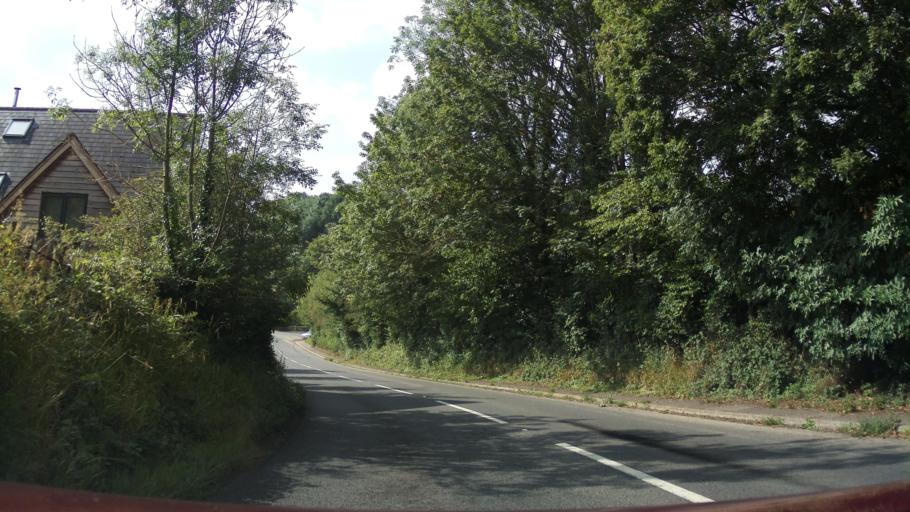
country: GB
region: England
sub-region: Somerset
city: Wincanton
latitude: 51.0612
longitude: -2.4146
